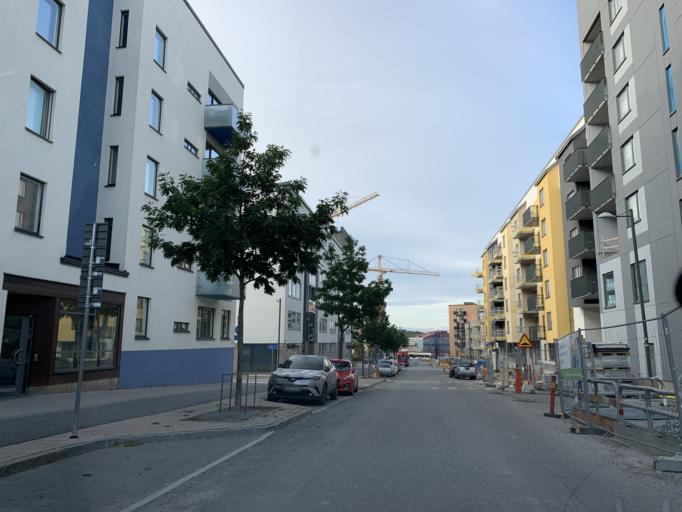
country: SE
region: Stockholm
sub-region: Sundbybergs Kommun
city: Sundbyberg
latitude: 59.3618
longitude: 17.9504
